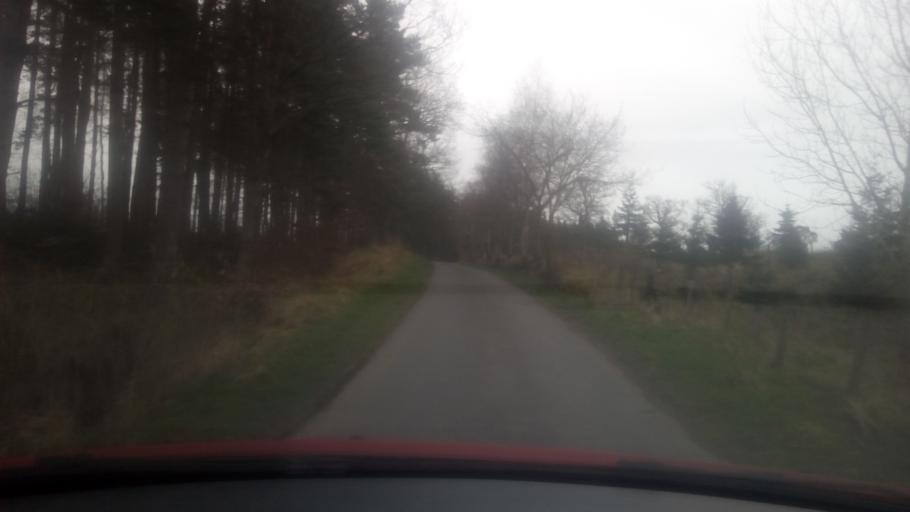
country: GB
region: Scotland
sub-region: The Scottish Borders
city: Jedburgh
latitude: 55.4417
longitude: -2.6419
